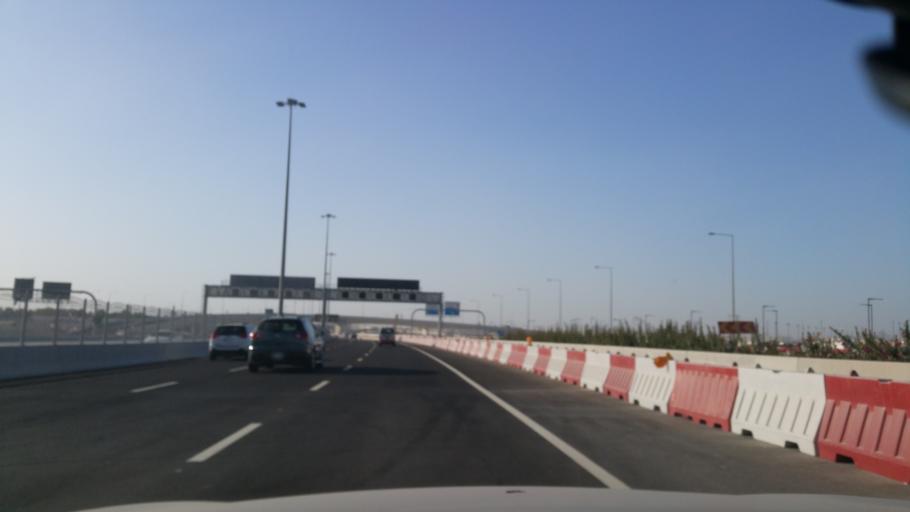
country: QA
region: Baladiyat ad Dawhah
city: Doha
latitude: 25.2312
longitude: 51.5302
